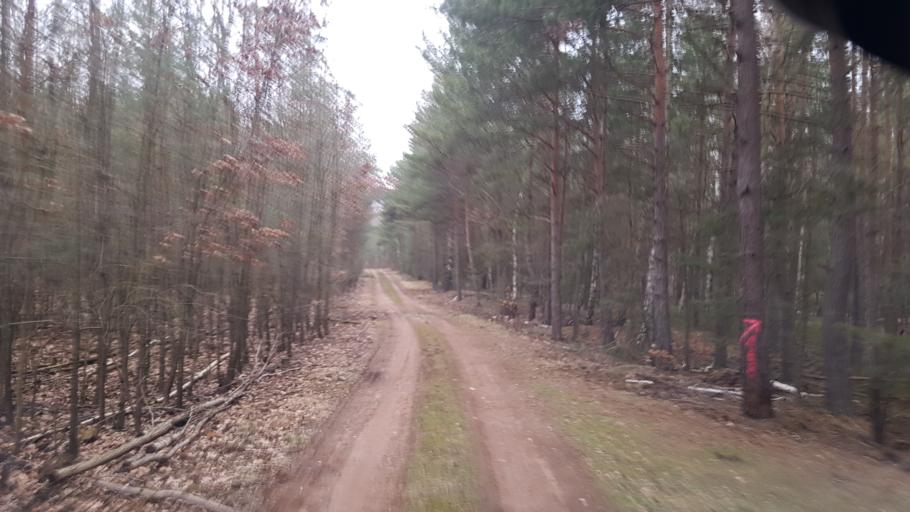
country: DE
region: Brandenburg
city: Trobitz
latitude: 51.6143
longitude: 13.4535
